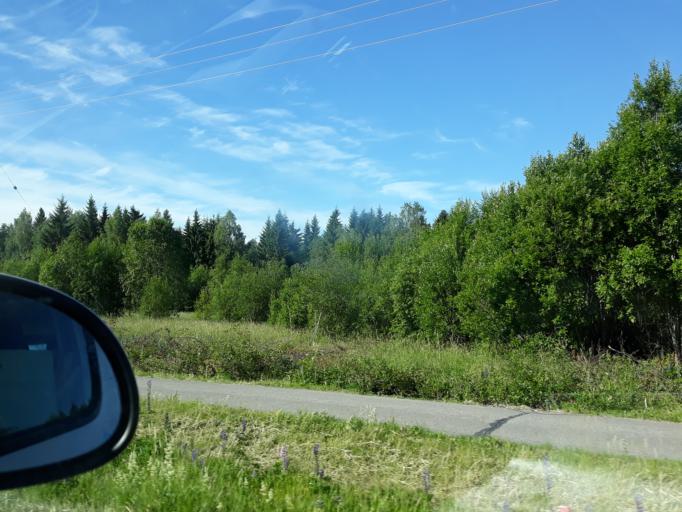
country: FI
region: Uusimaa
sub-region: Helsinki
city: Jaervenpaeae
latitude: 60.5438
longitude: 24.9865
